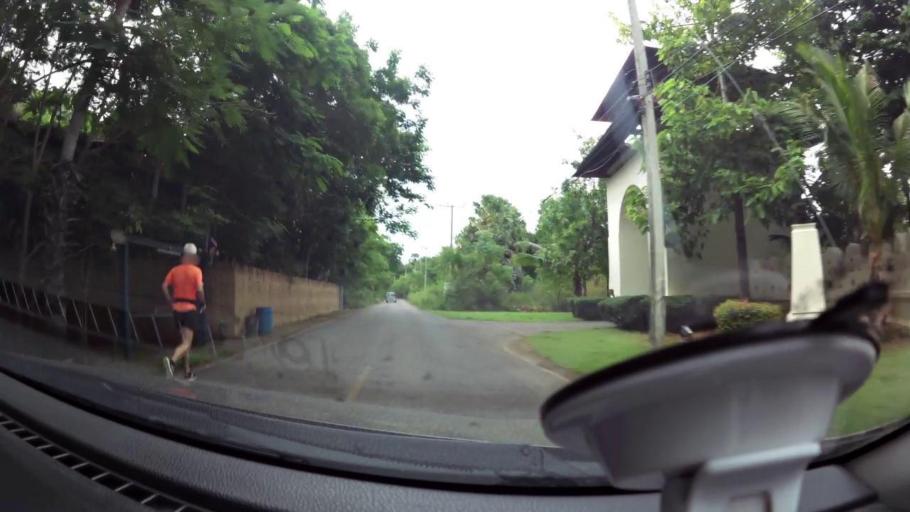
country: TH
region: Prachuap Khiri Khan
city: Pran Buri
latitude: 12.4262
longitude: 99.9796
